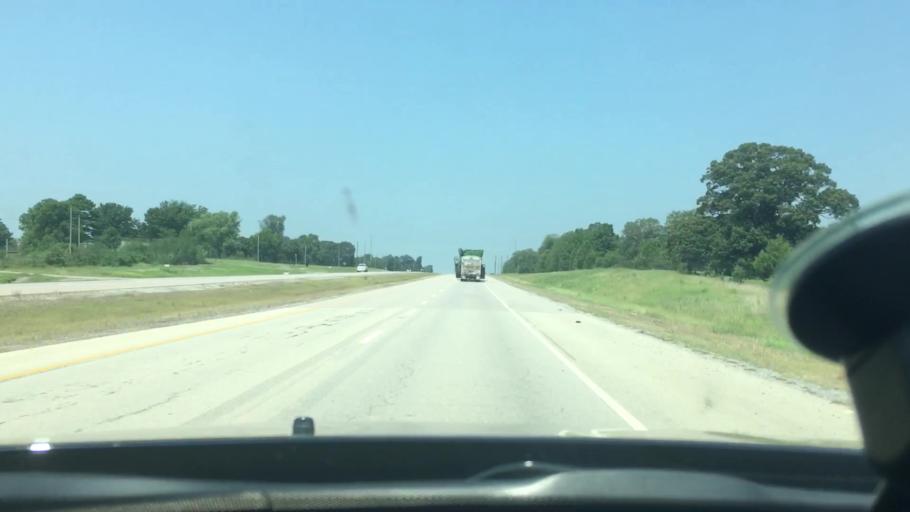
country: US
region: Oklahoma
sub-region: Atoka County
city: Atoka
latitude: 34.3252
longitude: -96.0427
